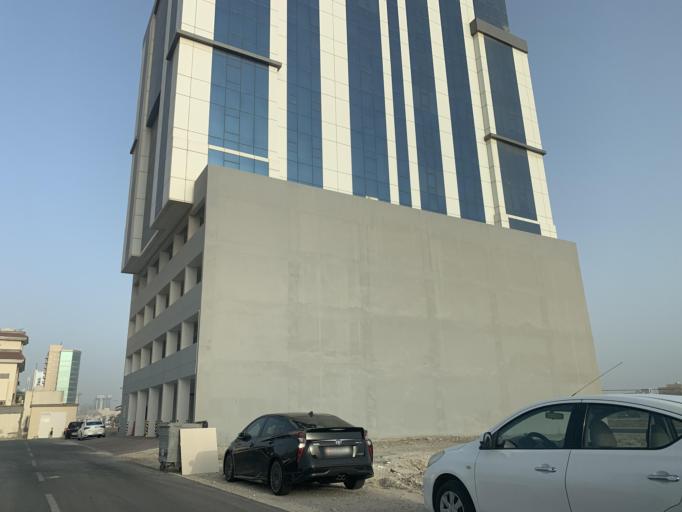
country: BH
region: Manama
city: Jidd Hafs
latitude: 26.2378
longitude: 50.5263
